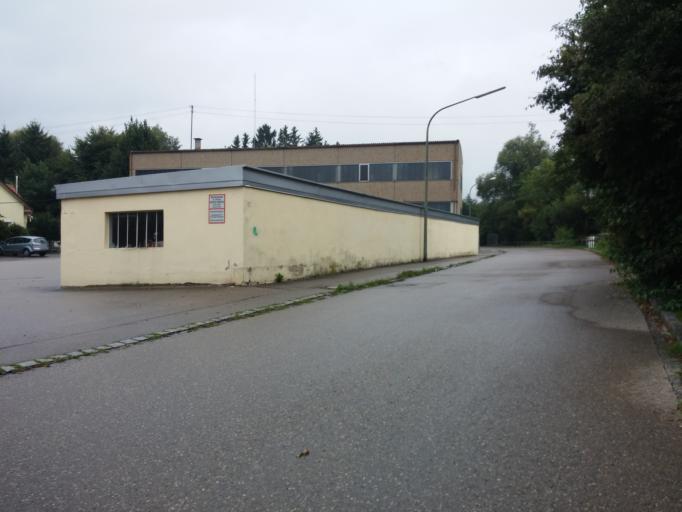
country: DE
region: Bavaria
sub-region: Swabia
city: Guenzburg
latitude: 48.4526
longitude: 10.2704
